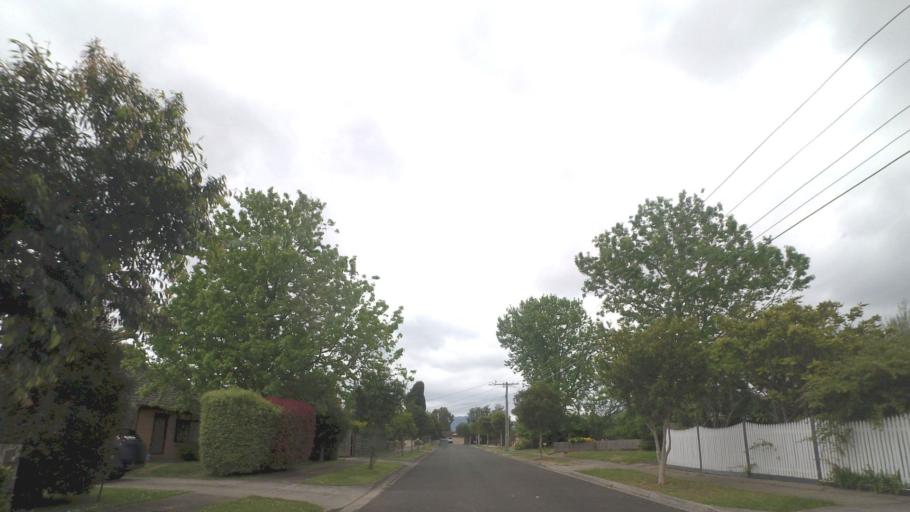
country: AU
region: Victoria
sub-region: Maroondah
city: Heathmont
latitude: -37.8441
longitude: 145.2518
